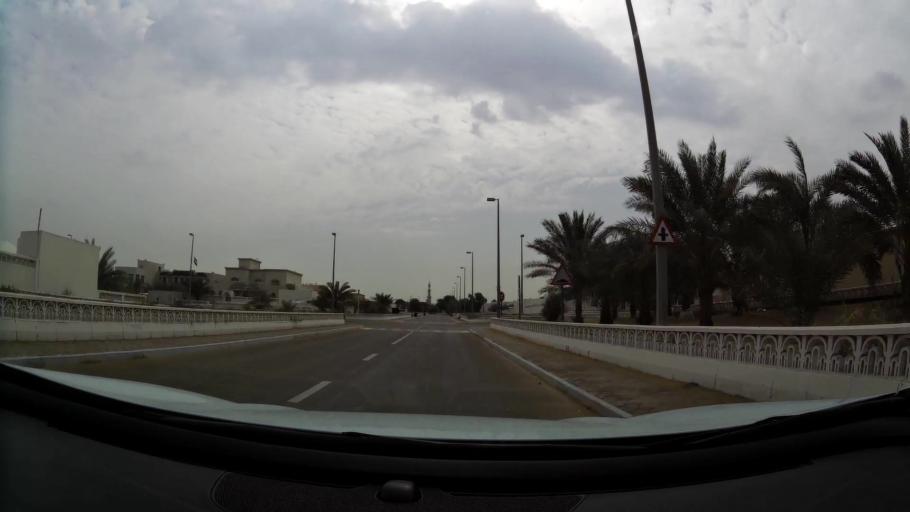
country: AE
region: Abu Dhabi
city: Abu Dhabi
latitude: 24.6345
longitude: 54.7176
